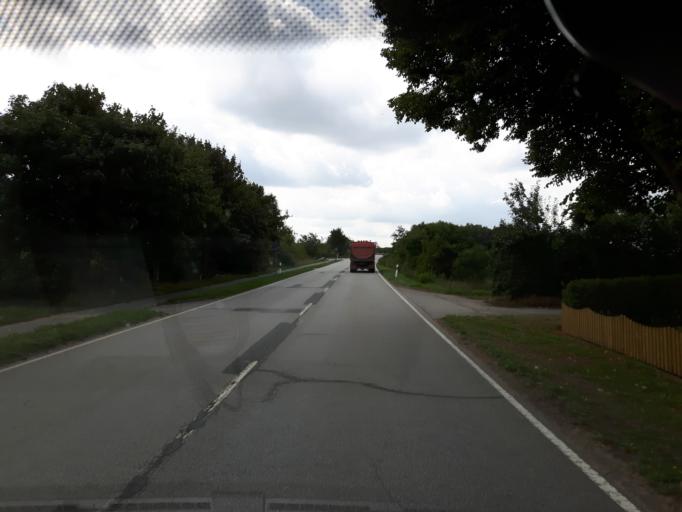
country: DE
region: Schleswig-Holstein
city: Handewitt
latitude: 54.7981
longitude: 9.3377
